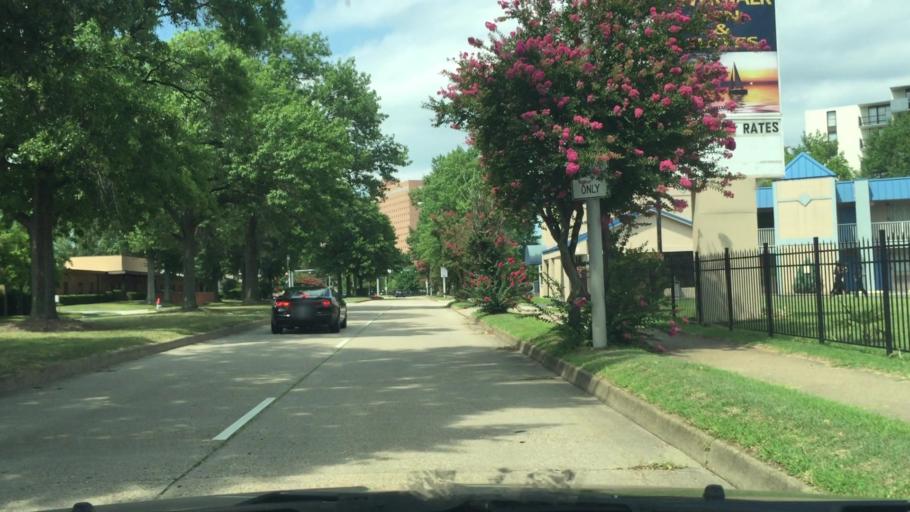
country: US
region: Virginia
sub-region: City of Portsmouth
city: Portsmouth
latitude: 36.8393
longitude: -76.3066
